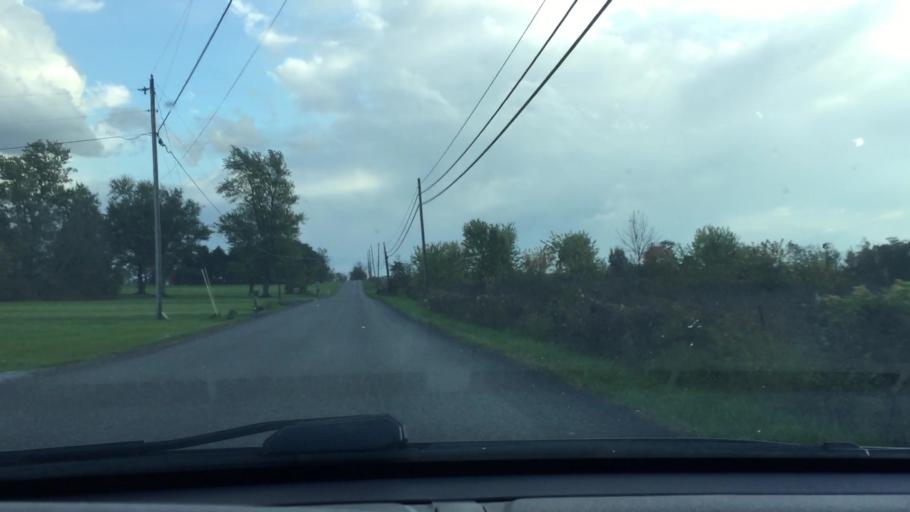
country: US
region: Pennsylvania
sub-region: Lawrence County
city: Bessemer
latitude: 40.9840
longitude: -80.4563
